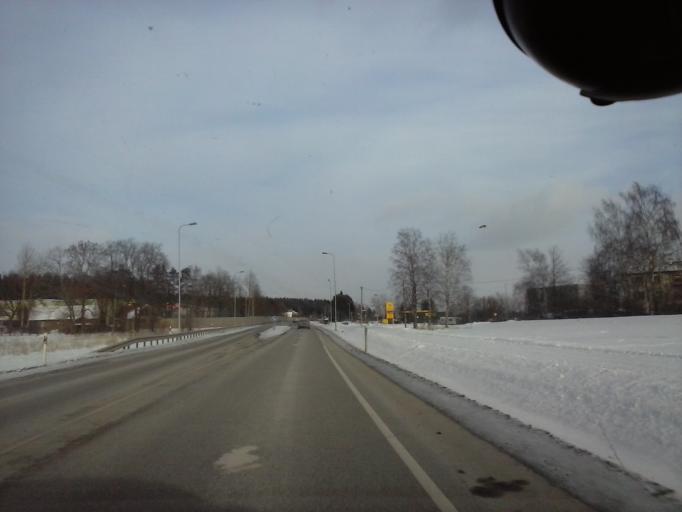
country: EE
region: Tartu
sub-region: Tartu linn
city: Tartu
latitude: 58.3557
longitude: 26.6164
